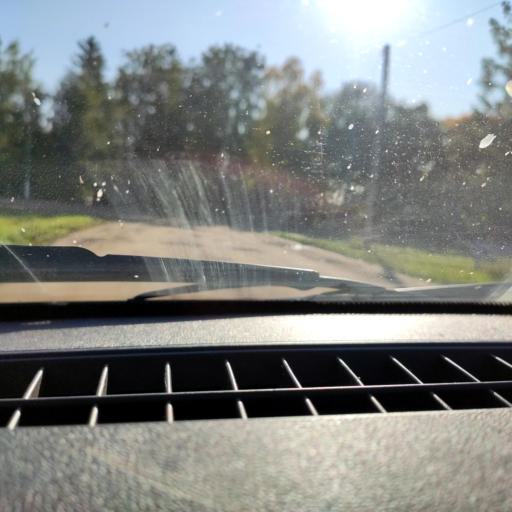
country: RU
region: Bashkortostan
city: Avdon
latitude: 54.5100
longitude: 55.7724
